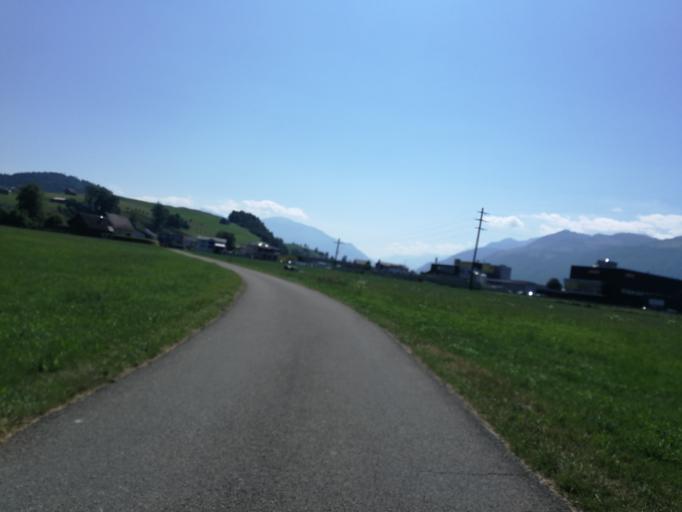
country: CH
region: Schwyz
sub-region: Bezirk March
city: Lachen
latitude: 47.1982
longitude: 8.8776
